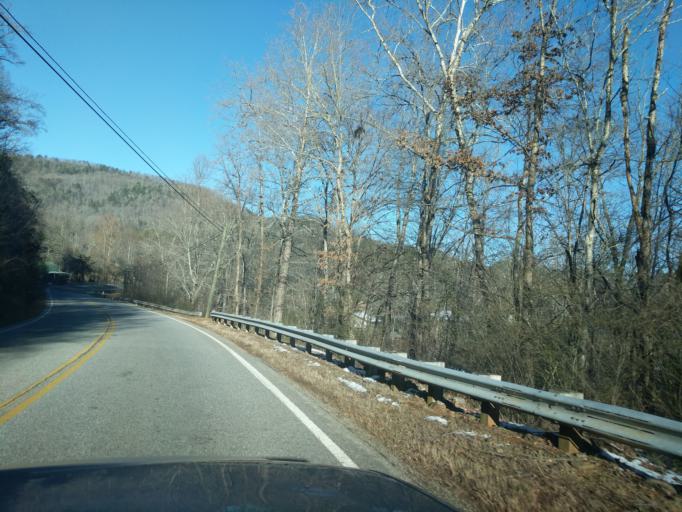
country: US
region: Georgia
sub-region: Towns County
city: Hiawassee
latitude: 34.9231
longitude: -83.6918
